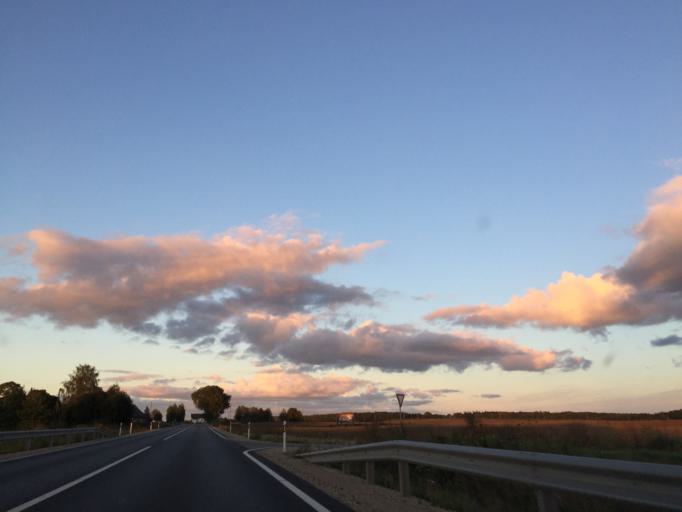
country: LV
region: Dobeles Rajons
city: Dobele
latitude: 56.7053
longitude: 23.1752
